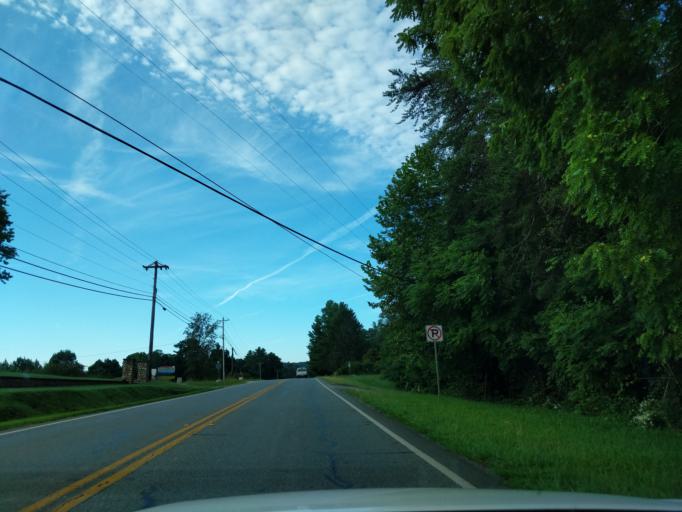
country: US
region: Georgia
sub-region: Fannin County
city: McCaysville
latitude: 34.9564
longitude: -84.3675
